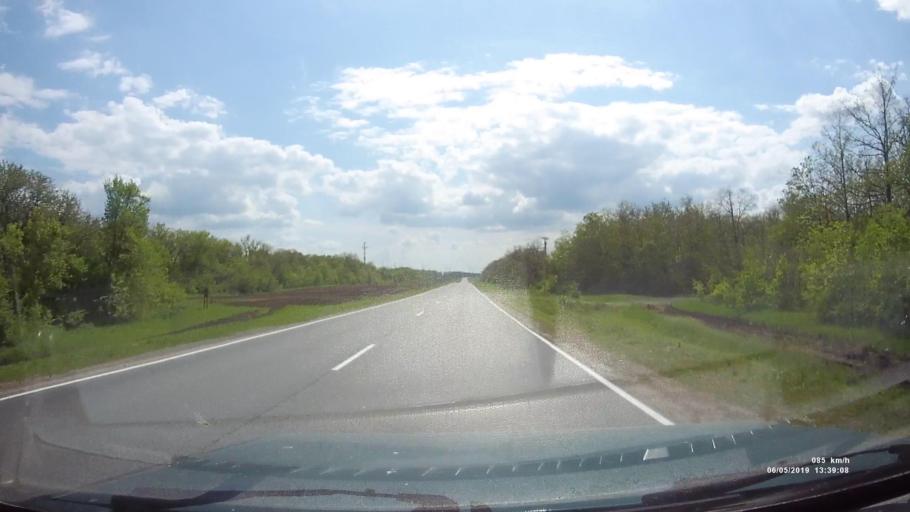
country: RU
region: Rostov
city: Ust'-Donetskiy
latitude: 47.6794
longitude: 40.7052
